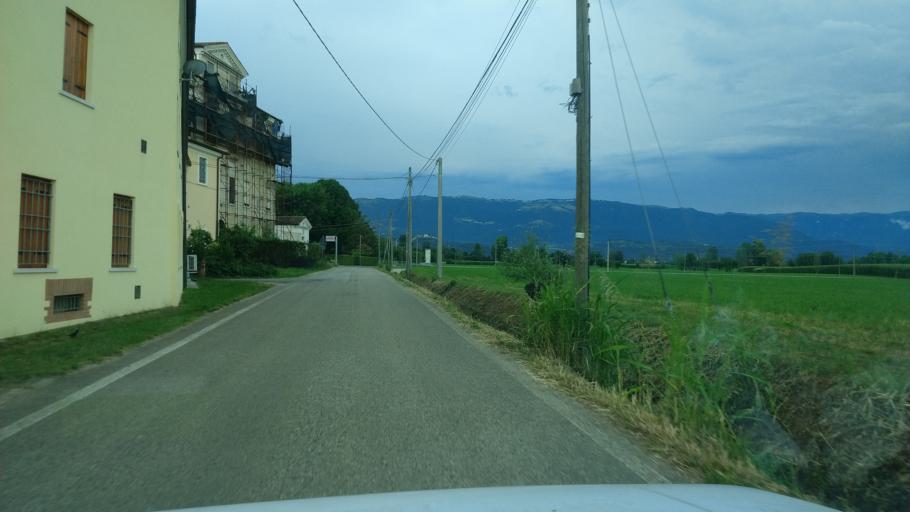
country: IT
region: Veneto
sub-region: Provincia di Vicenza
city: Nove
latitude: 45.7141
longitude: 11.6599
